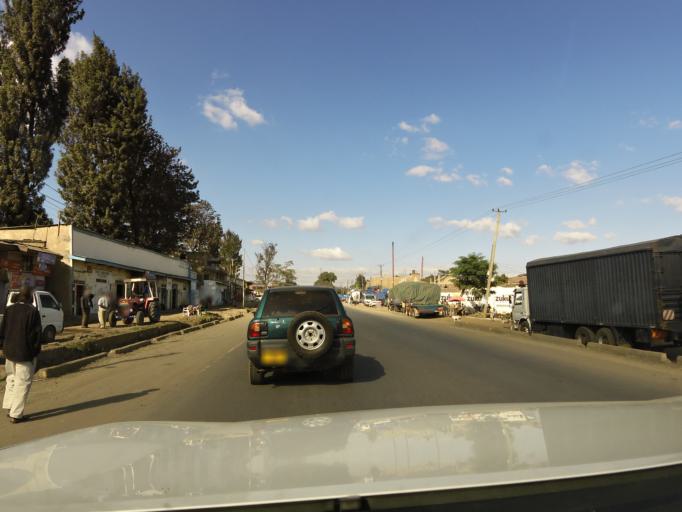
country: TZ
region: Arusha
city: Arusha
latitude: -3.3761
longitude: 36.6606
